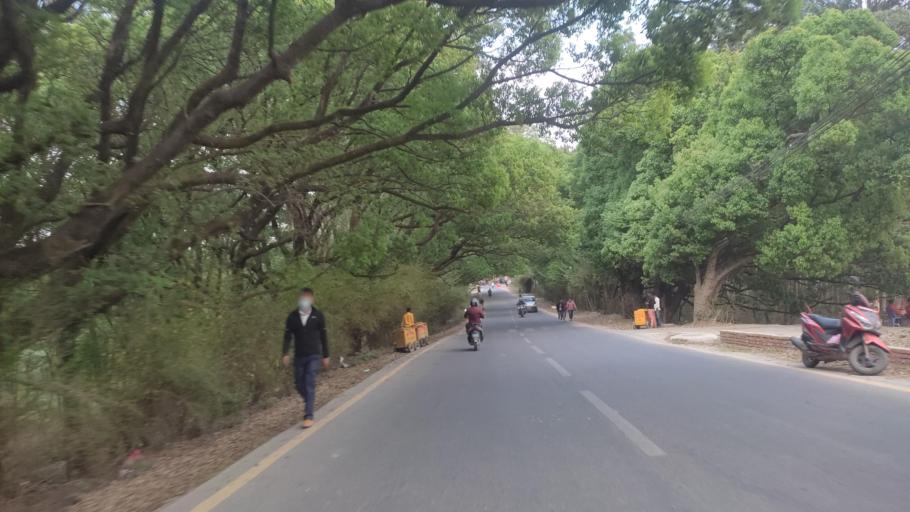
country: NP
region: Central Region
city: Kirtipur
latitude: 27.6793
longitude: 85.2906
